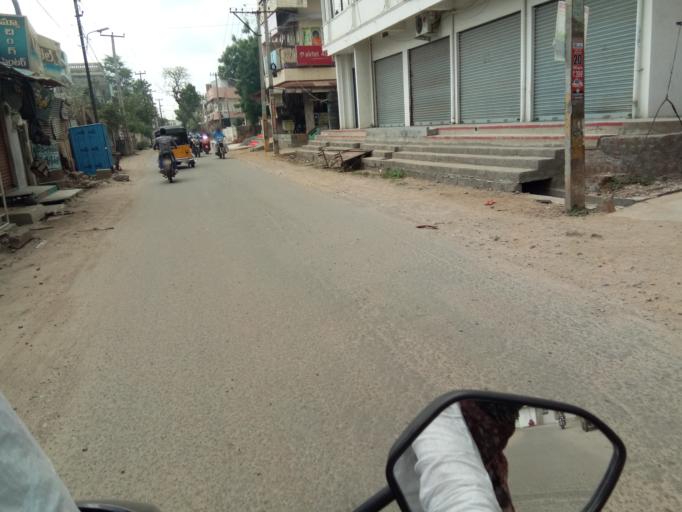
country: IN
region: Telangana
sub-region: Khammam
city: Khammam
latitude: 17.2382
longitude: 80.1453
